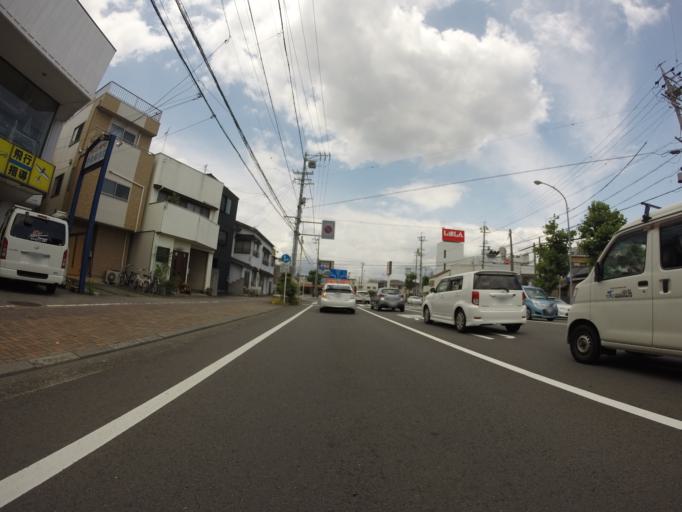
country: JP
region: Shizuoka
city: Shizuoka-shi
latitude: 34.9632
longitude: 138.3717
